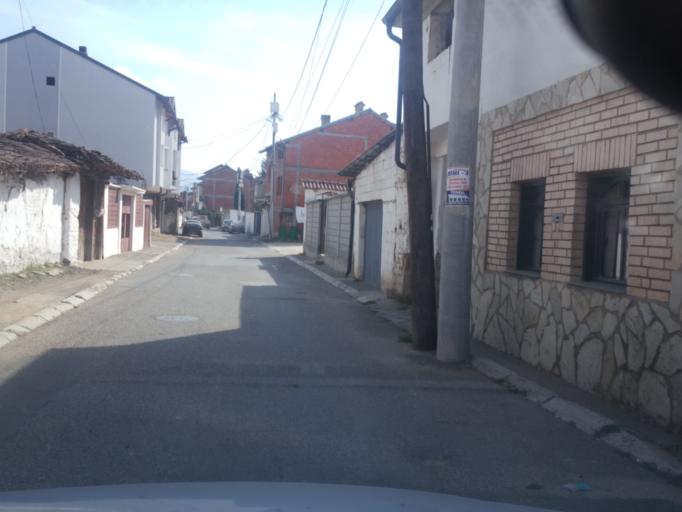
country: XK
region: Gjakova
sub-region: Komuna e Gjakoves
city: Gjakove
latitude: 42.3815
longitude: 20.4243
